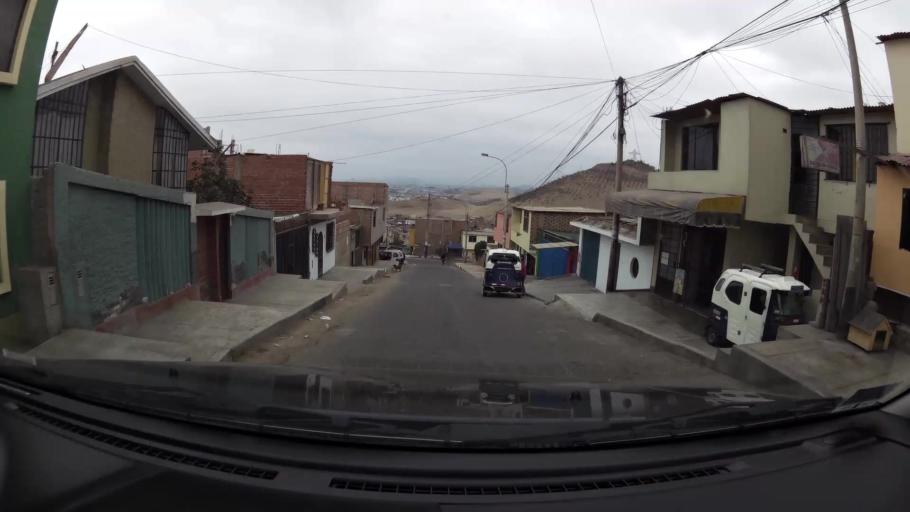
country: PE
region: Lima
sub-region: Lima
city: Surco
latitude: -12.1883
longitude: -76.9903
